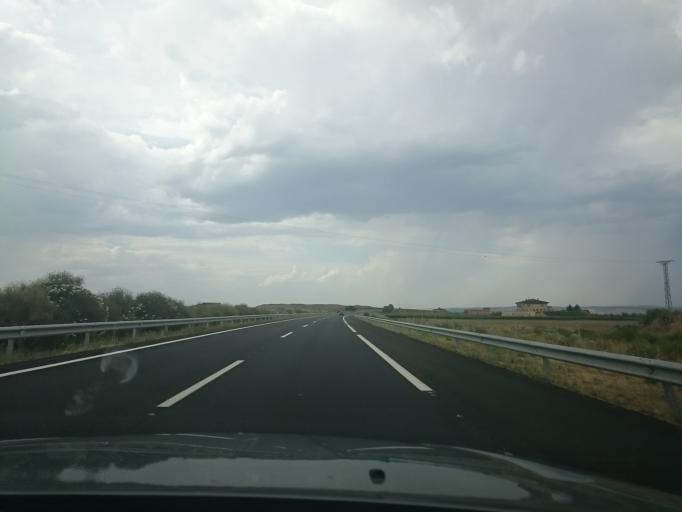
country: ES
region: La Rioja
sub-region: Provincia de La Rioja
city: Aldeanueva de Ebro
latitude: 42.2256
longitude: -1.8980
